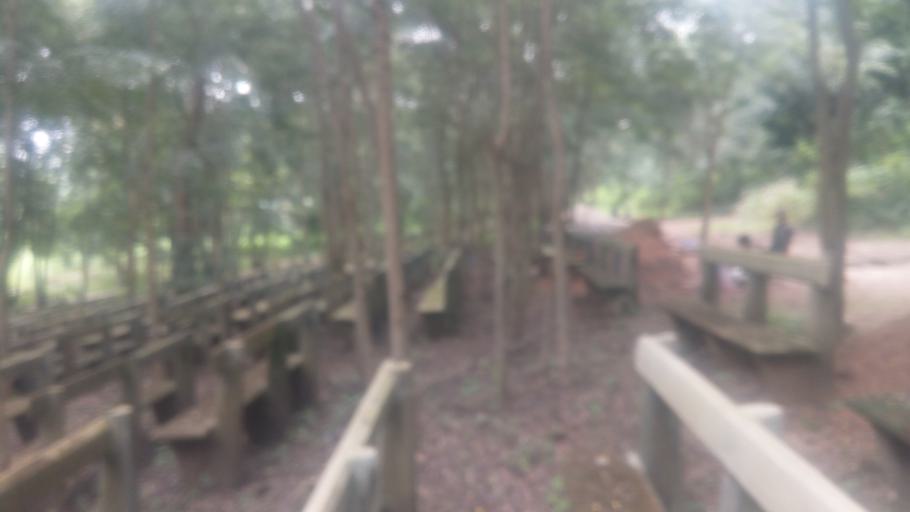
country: TG
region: Plateaux
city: Kpalime
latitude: 7.0085
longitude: 0.6533
